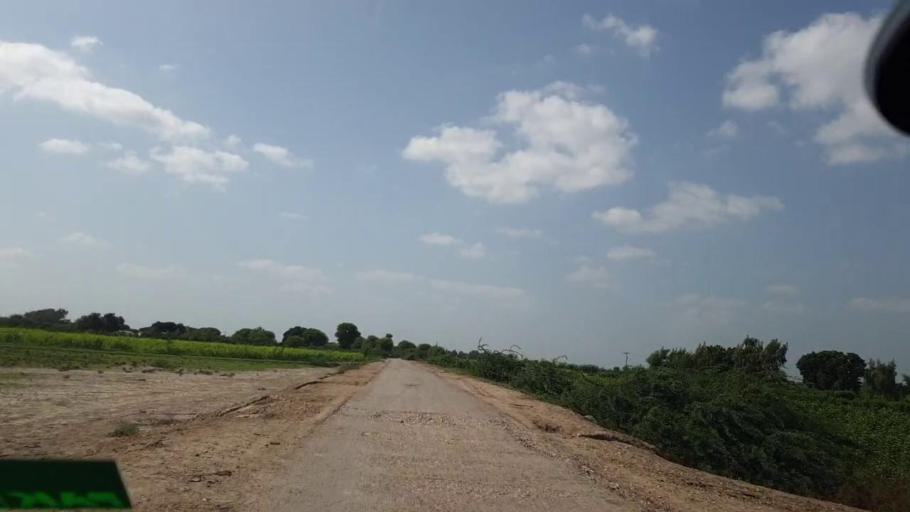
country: PK
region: Sindh
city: Naukot
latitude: 24.6518
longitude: 69.2174
